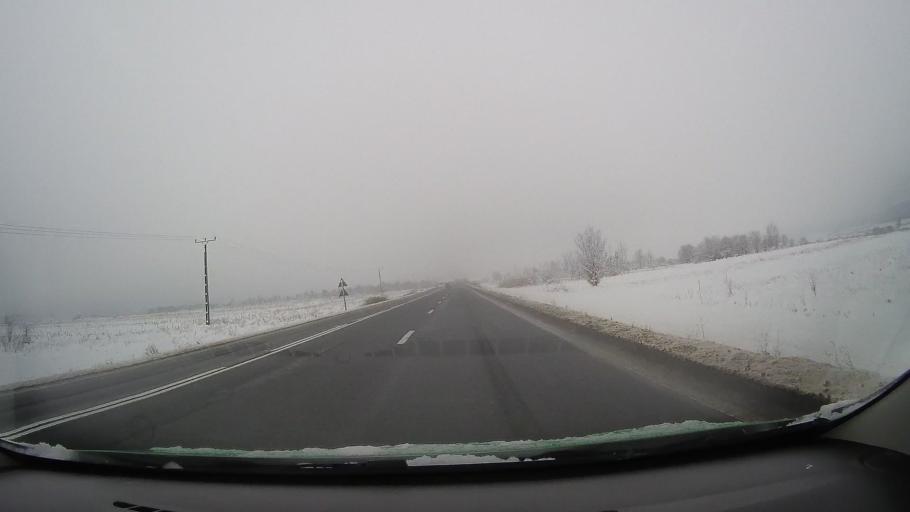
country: RO
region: Sibiu
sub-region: Oras Saliste
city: Saliste
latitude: 45.7894
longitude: 23.9258
